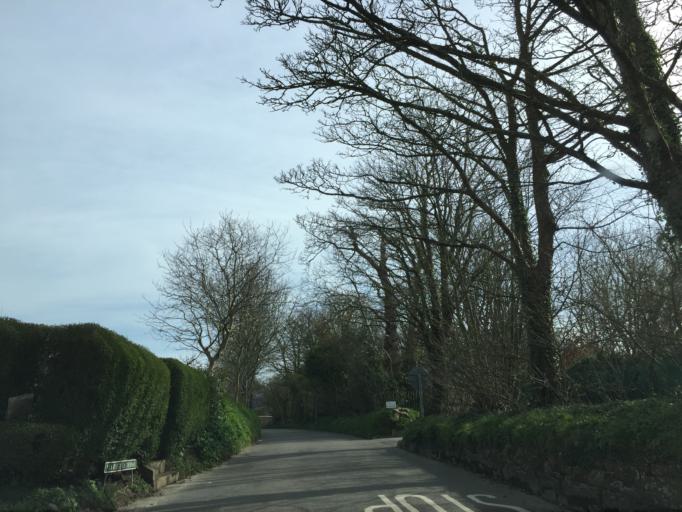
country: JE
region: St Helier
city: Saint Helier
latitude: 49.2278
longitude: -2.1148
